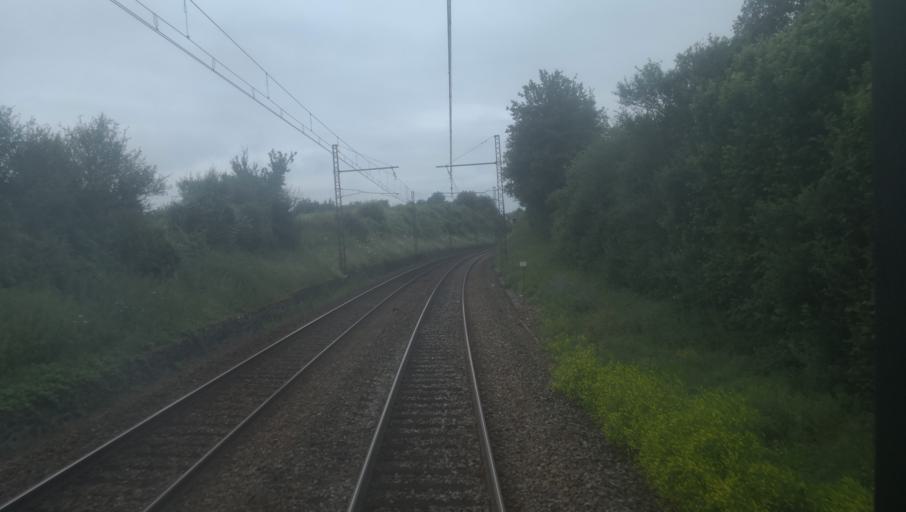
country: FR
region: Centre
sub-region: Departement de l'Indre
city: Le Pechereau
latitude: 46.5025
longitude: 1.5045
